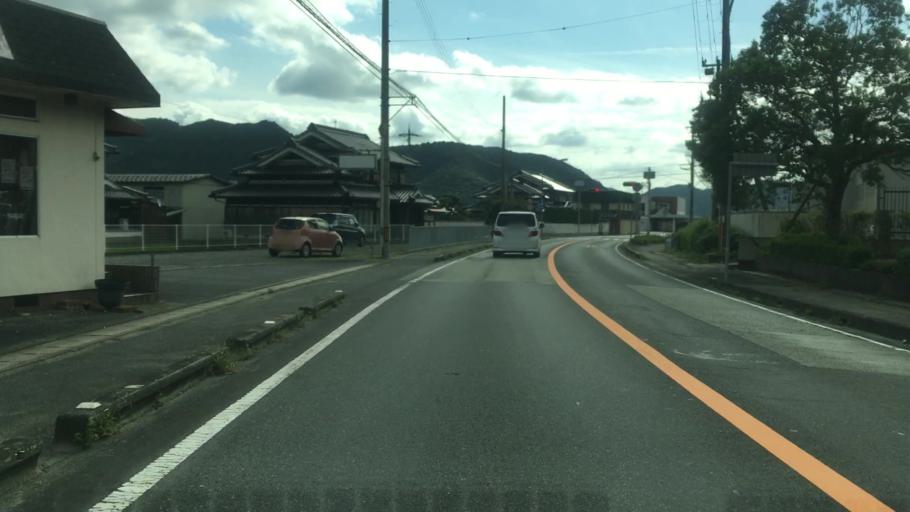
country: JP
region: Kyoto
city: Fukuchiyama
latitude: 35.2484
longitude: 135.0052
